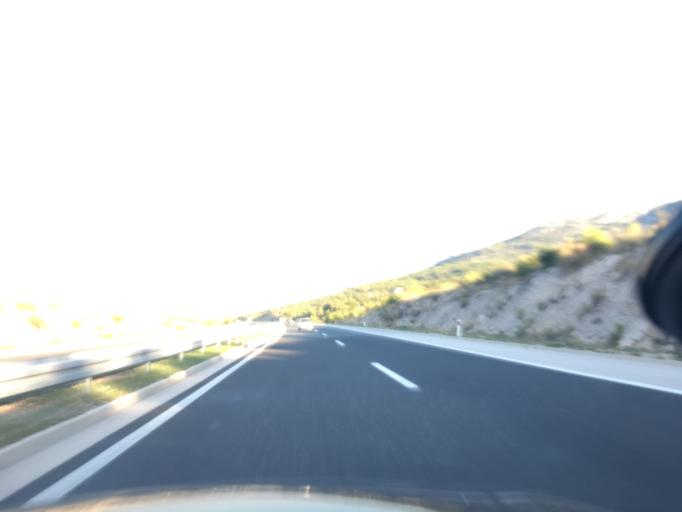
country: HR
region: Sibensko-Kniniska
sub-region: Grad Sibenik
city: Sibenik
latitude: 43.7480
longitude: 15.9559
